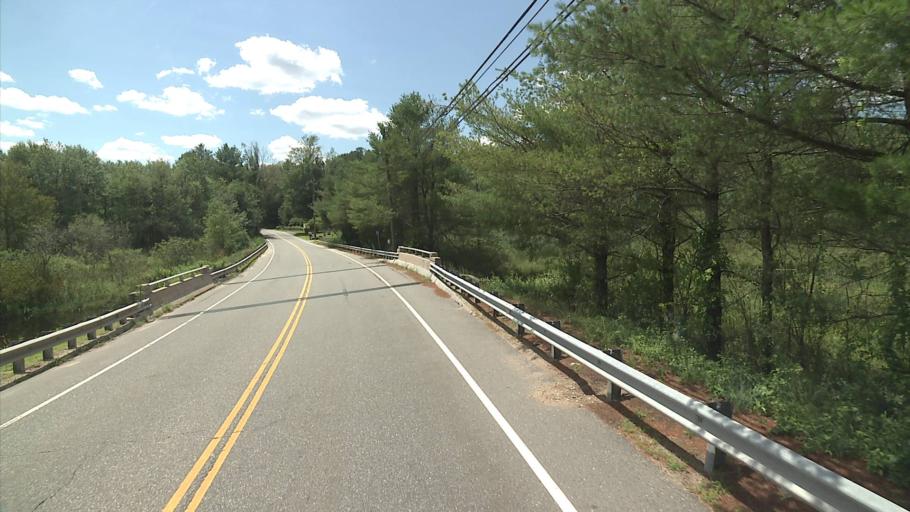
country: US
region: Connecticut
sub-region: Windham County
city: Quinebaug
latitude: 41.9964
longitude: -71.9896
